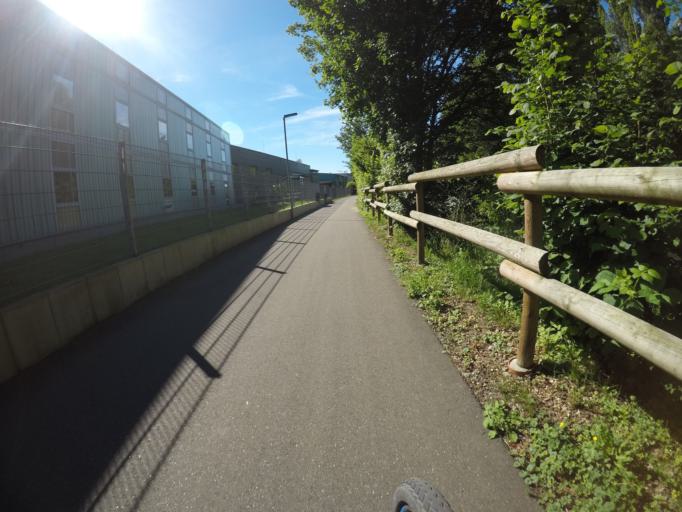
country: DE
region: Baden-Wuerttemberg
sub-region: Karlsruhe Region
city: Joehlingen
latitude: 48.9950
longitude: 8.5374
